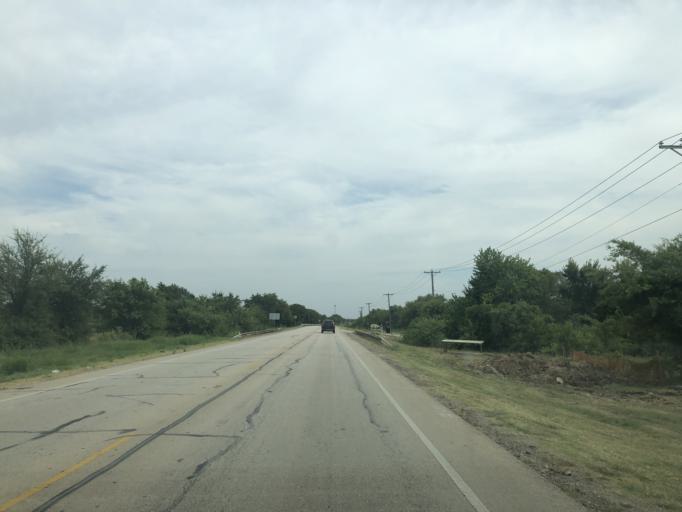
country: US
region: Texas
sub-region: Tarrant County
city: Saginaw
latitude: 32.8914
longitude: -97.3469
